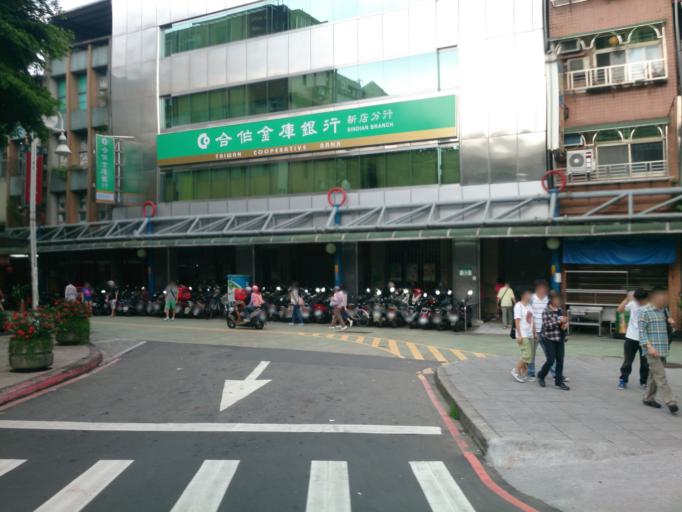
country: TW
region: Taipei
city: Taipei
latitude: 24.9589
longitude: 121.5381
